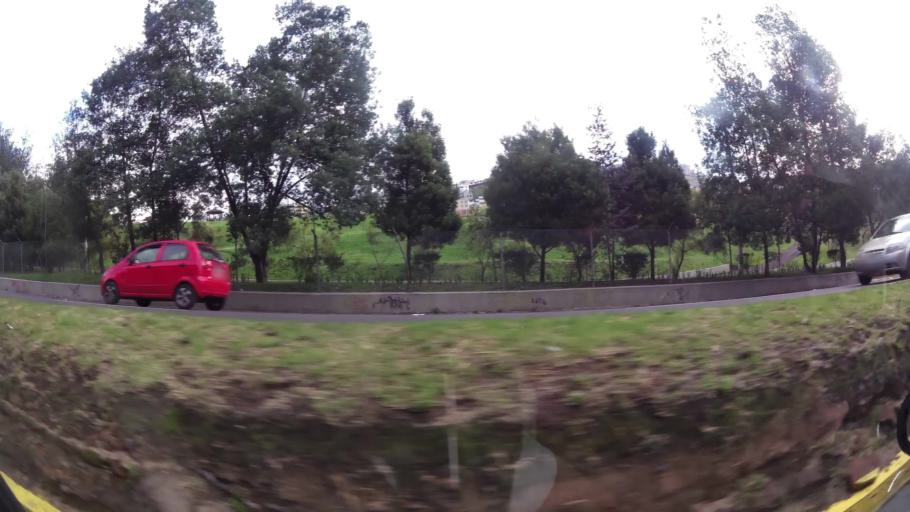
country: EC
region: Pichincha
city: Quito
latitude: -0.2286
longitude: -78.4856
